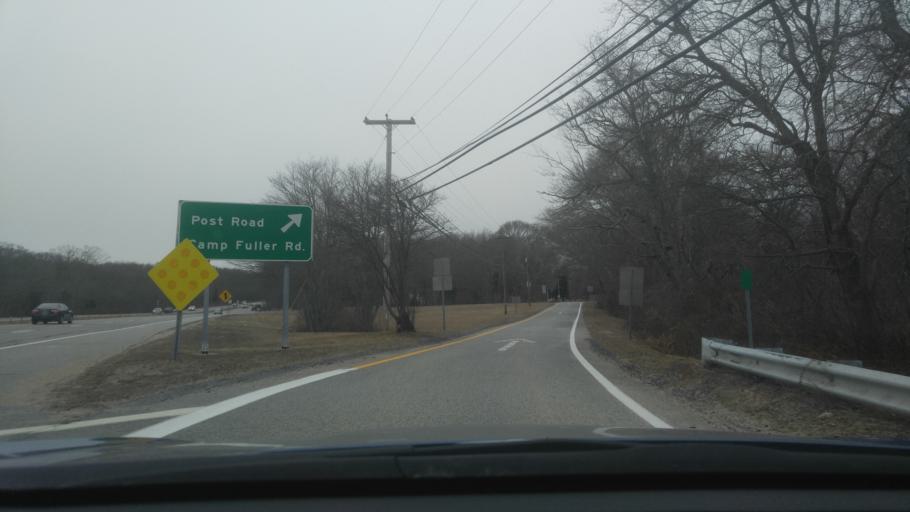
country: US
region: Rhode Island
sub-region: Washington County
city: Wakefield-Peacedale
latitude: 41.4120
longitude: -71.5308
